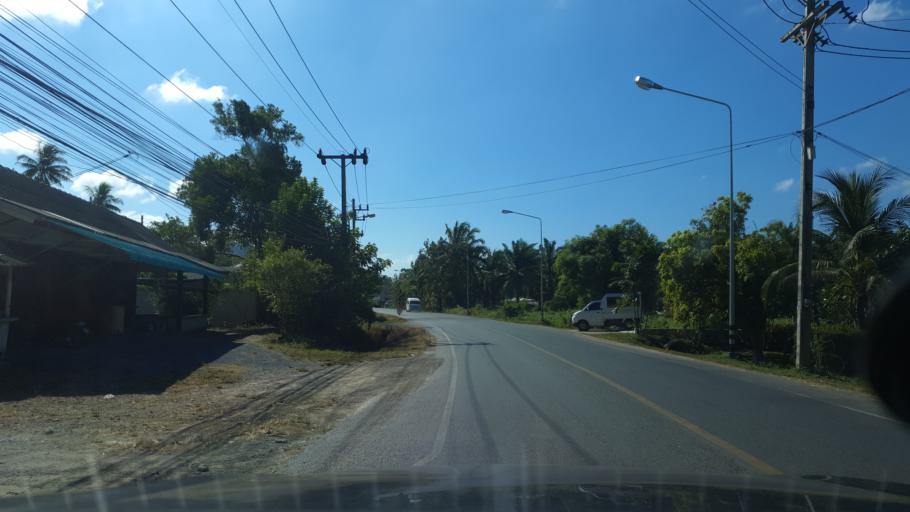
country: TH
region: Phangnga
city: Ban Ao Nang
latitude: 8.0574
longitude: 98.8145
